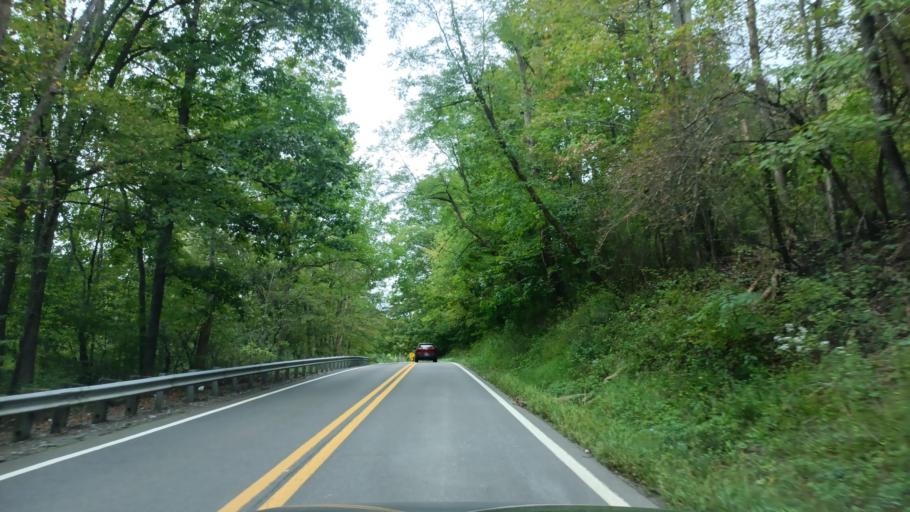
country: US
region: West Virginia
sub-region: Taylor County
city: Grafton
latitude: 39.3347
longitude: -79.8768
